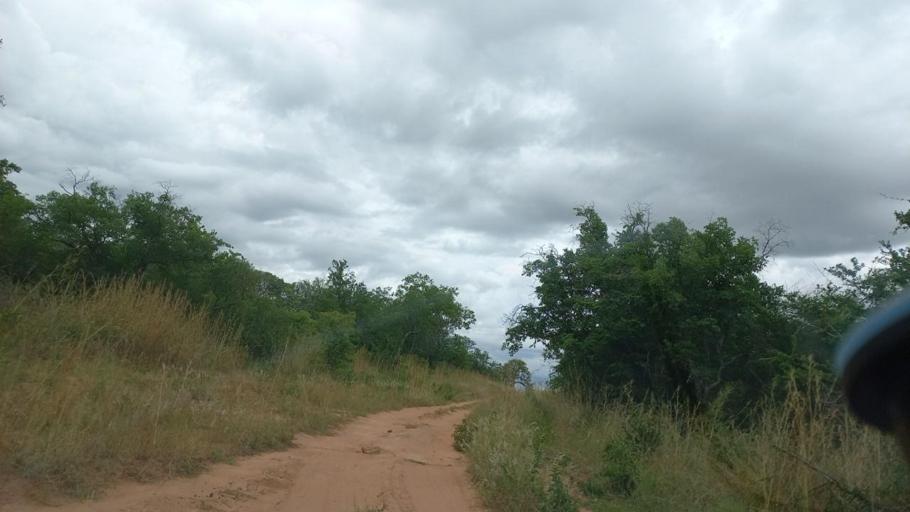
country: ZM
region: Lusaka
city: Luangwa
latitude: -15.5666
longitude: 30.3226
